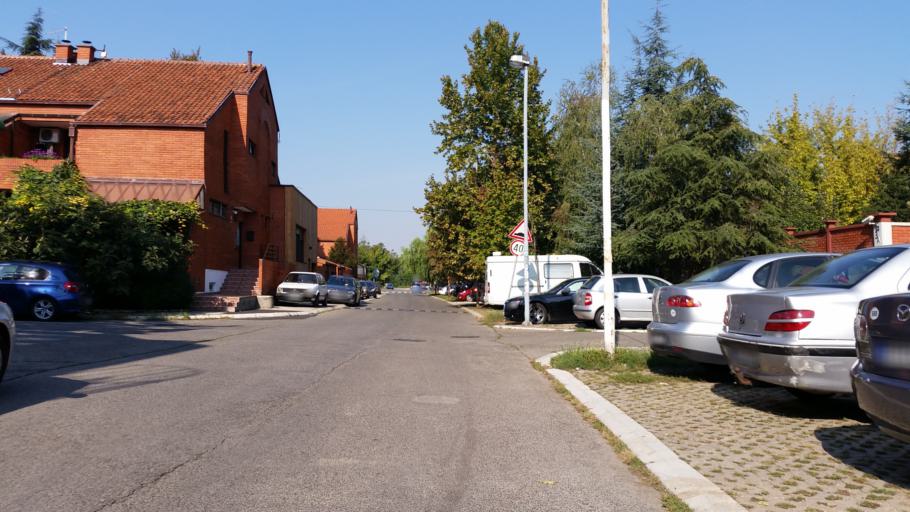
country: RS
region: Central Serbia
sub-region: Belgrade
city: Zemun
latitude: 44.8228
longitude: 20.3909
